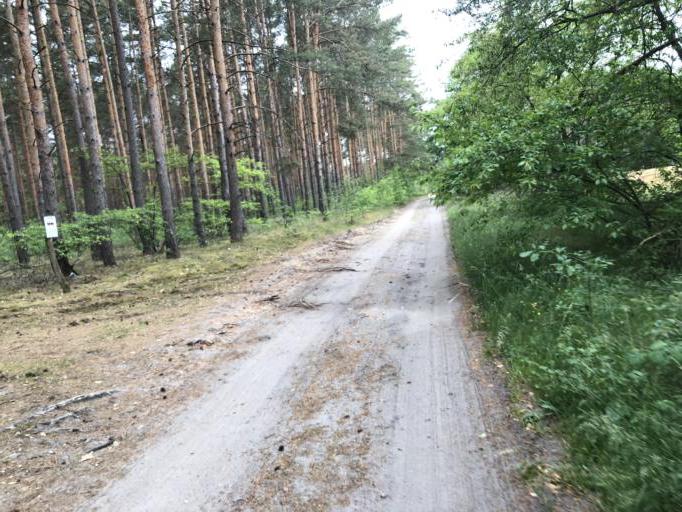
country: DE
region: Brandenburg
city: Gross Koris
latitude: 52.1933
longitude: 13.6426
